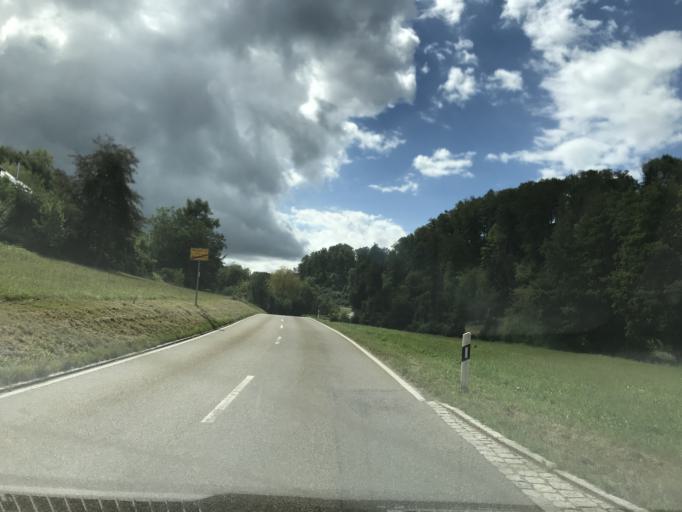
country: DE
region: Baden-Wuerttemberg
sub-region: Freiburg Region
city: Maulburg
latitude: 47.6382
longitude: 7.7776
